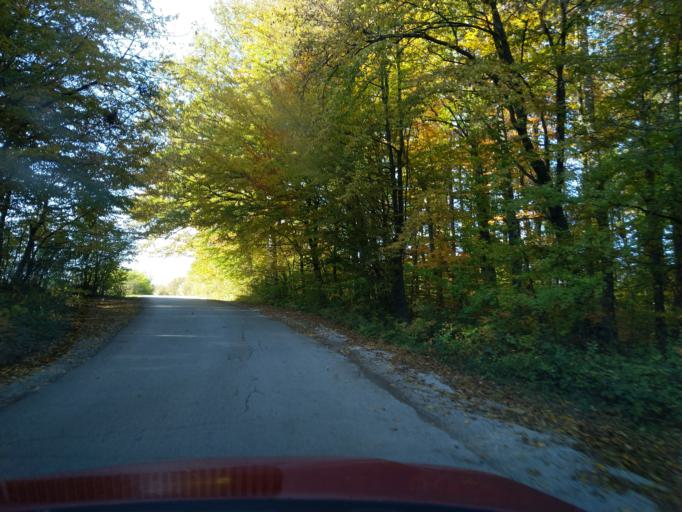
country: RS
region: Central Serbia
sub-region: Zlatiborski Okrug
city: Uzice
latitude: 43.8640
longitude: 19.7676
